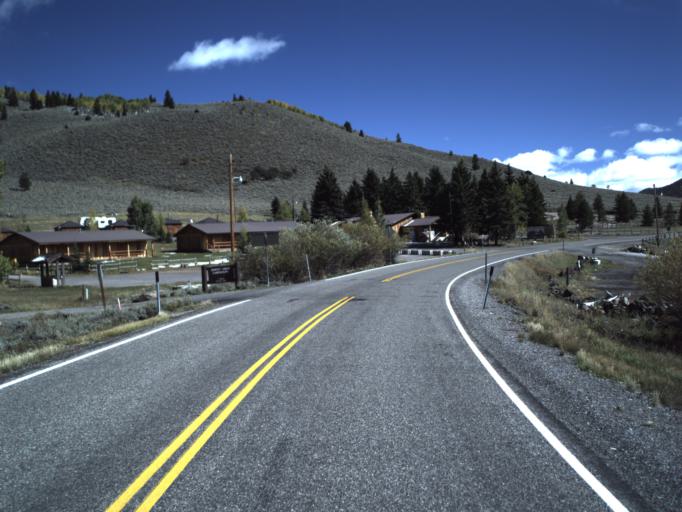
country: US
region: Utah
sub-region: Wayne County
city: Loa
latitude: 38.5620
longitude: -111.7072
